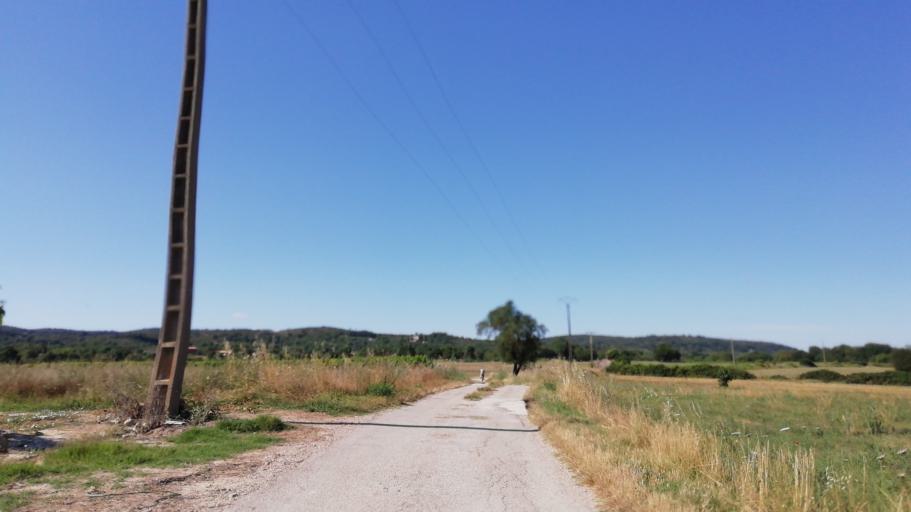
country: FR
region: Languedoc-Roussillon
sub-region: Departement de l'Herault
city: Saint-Martin-de-Londres
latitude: 43.7945
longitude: 3.7560
